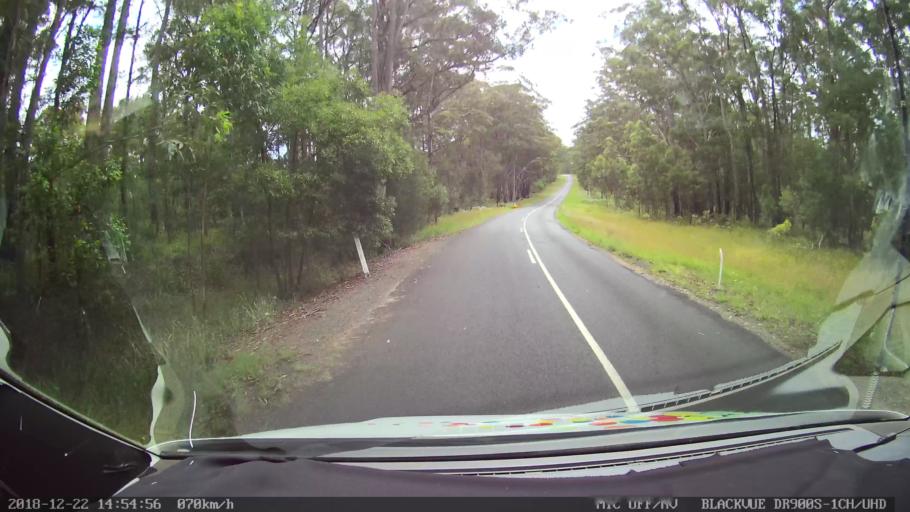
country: AU
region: New South Wales
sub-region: Bellingen
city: Dorrigo
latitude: -30.2289
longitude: 152.5277
